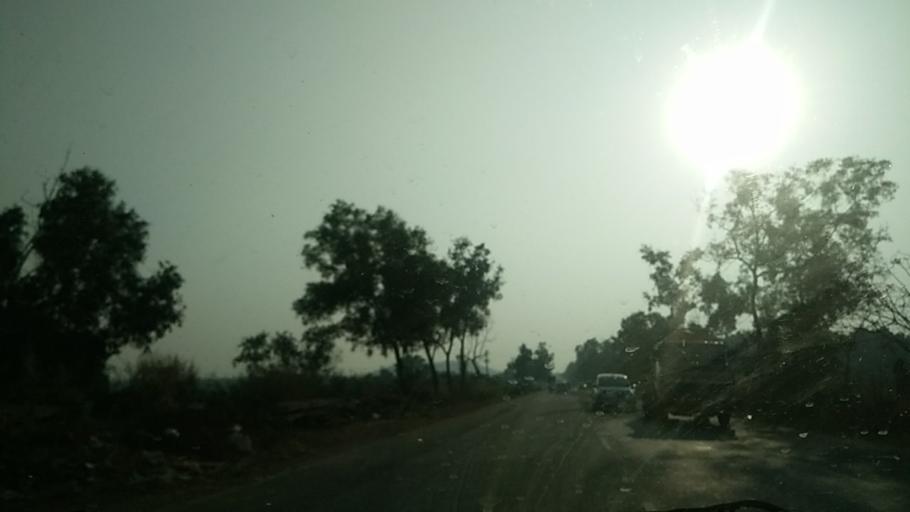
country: IN
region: Goa
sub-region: North Goa
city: Guirim
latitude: 15.5781
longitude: 73.8108
